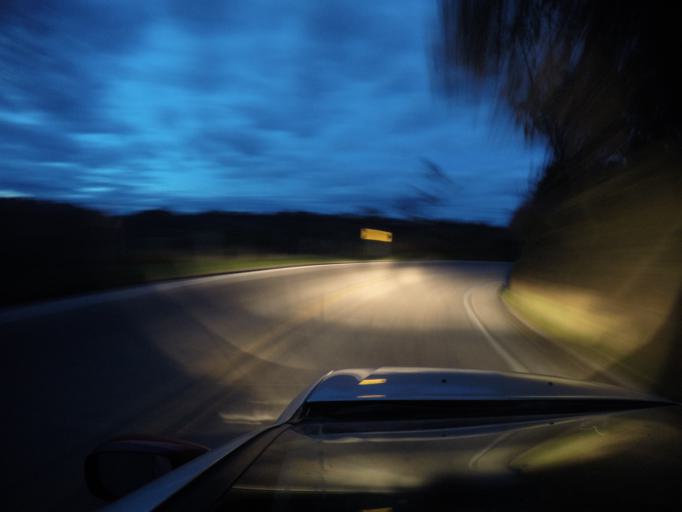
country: CO
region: Tolima
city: Fresno
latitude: 5.1599
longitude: -75.0886
